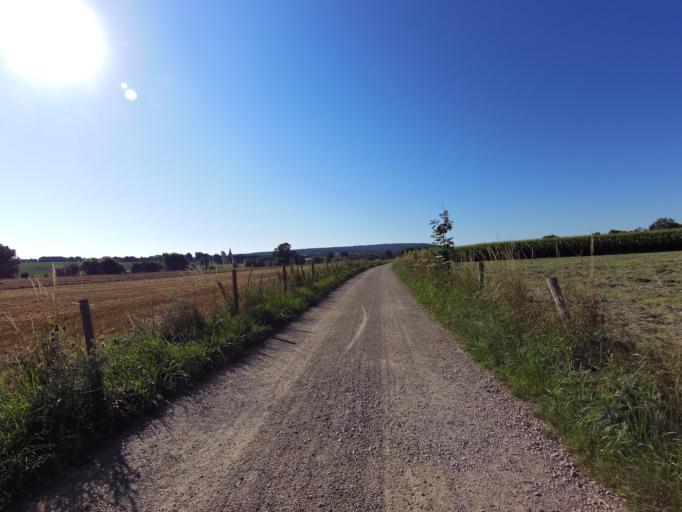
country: NL
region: Limburg
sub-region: Gemeente Voerendaal
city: Ubachsberg
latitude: 50.8007
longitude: 5.9155
